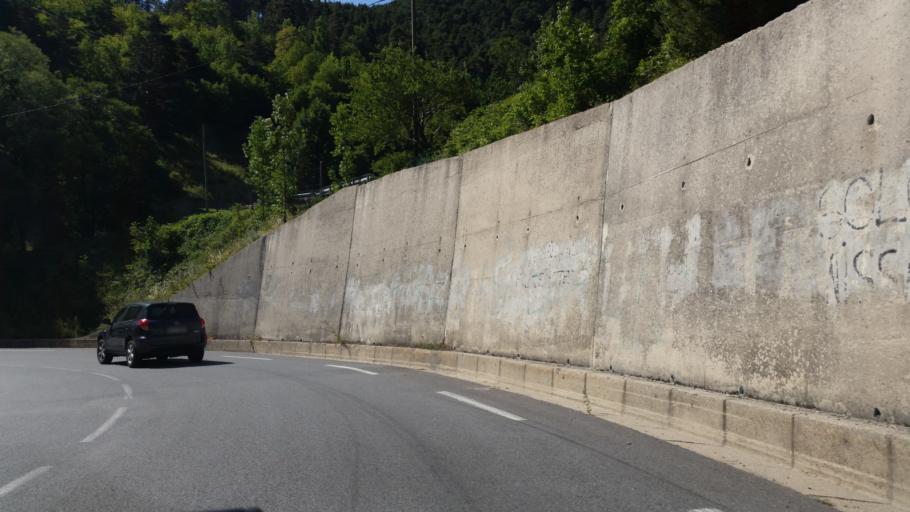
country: FR
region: Provence-Alpes-Cote d'Azur
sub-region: Departement des Alpes-Maritimes
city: Tende
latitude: 44.1272
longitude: 7.5625
